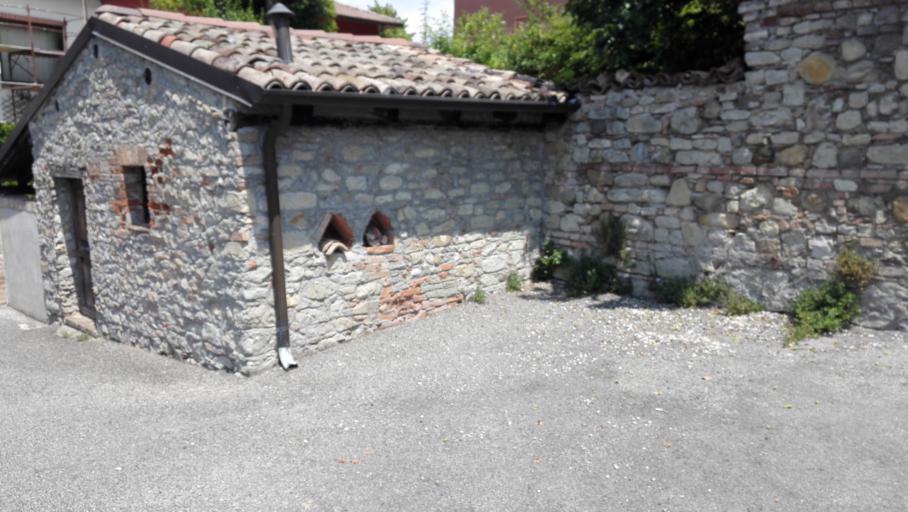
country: IT
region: Piedmont
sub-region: Provincia di Alessandria
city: Sant'Agata Fossili
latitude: 44.7857
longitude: 8.9208
